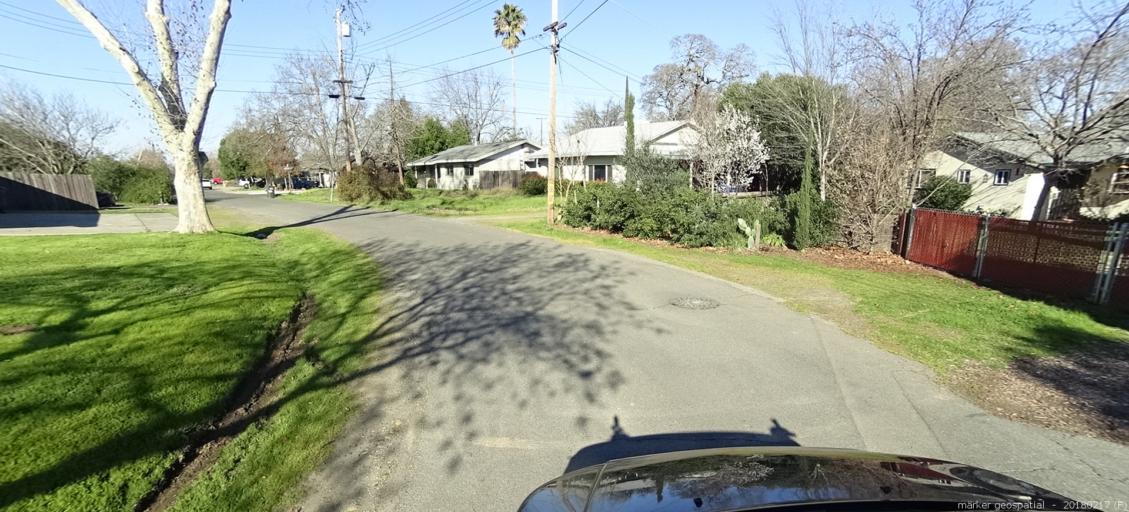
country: US
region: California
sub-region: Sacramento County
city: Folsom
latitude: 38.6703
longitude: -121.1973
